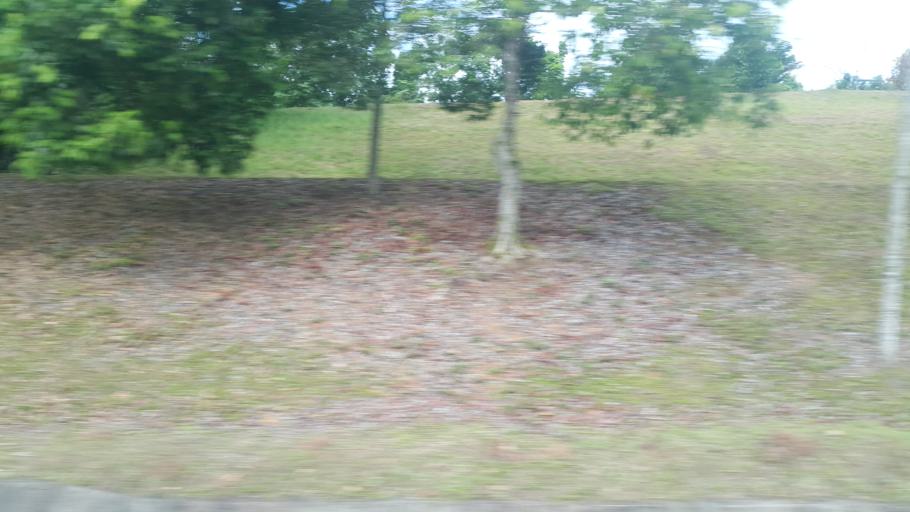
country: MY
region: Johor
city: Skudai
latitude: 1.4949
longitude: 103.6099
